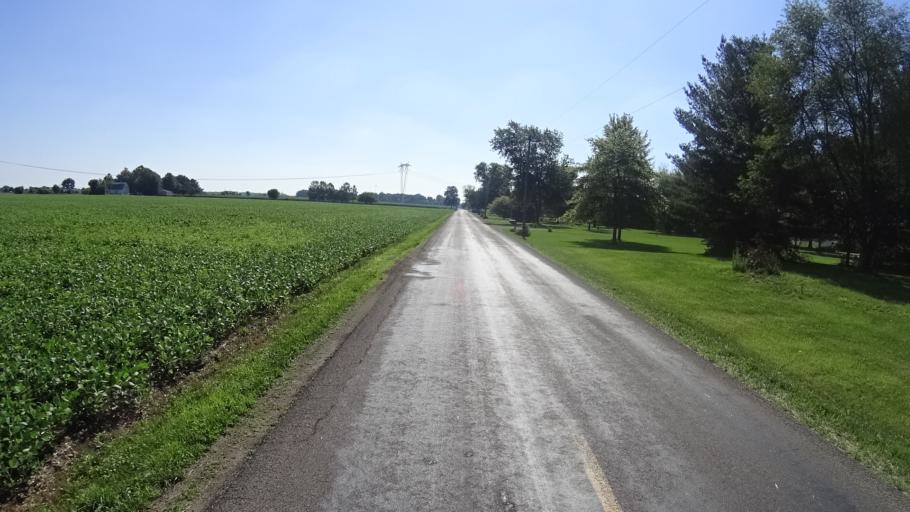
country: US
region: Indiana
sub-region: Madison County
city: Ingalls
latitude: 39.9878
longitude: -85.8199
